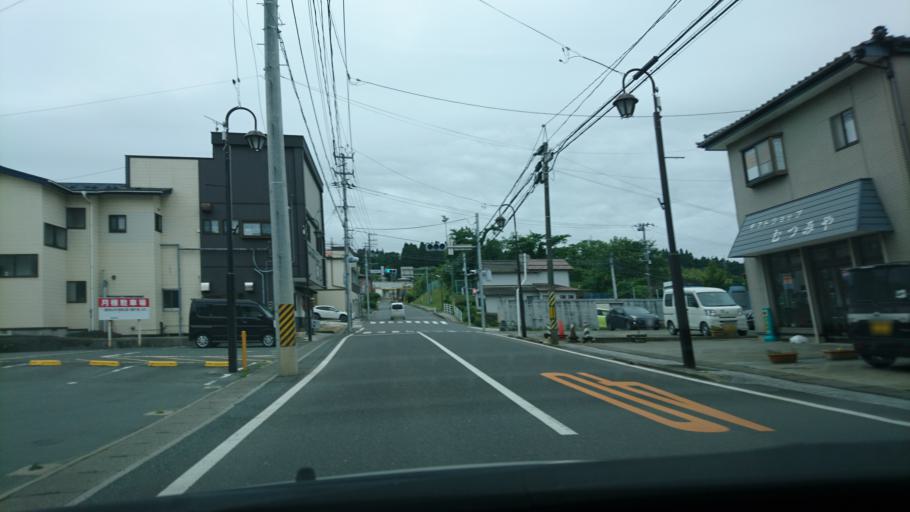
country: JP
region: Iwate
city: Ofunato
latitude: 38.7899
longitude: 141.5052
